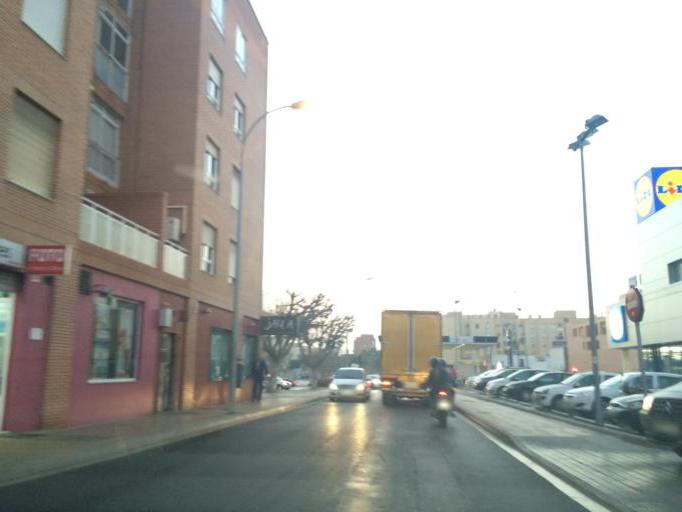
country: ES
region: Andalusia
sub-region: Provincia de Almeria
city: Almeria
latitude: 36.8352
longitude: -2.4459
